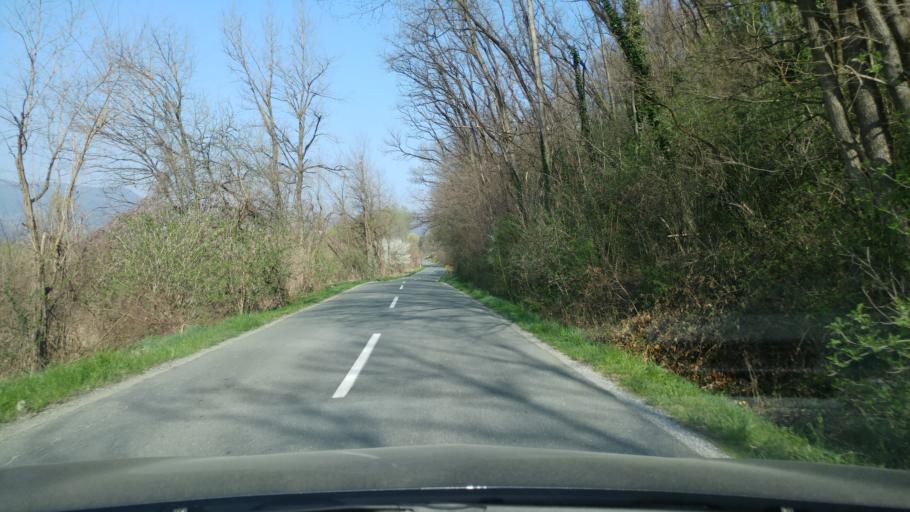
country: SI
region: Bistrica ob Sotli
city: Bistrica ob Sotli
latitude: 46.0001
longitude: 15.7182
